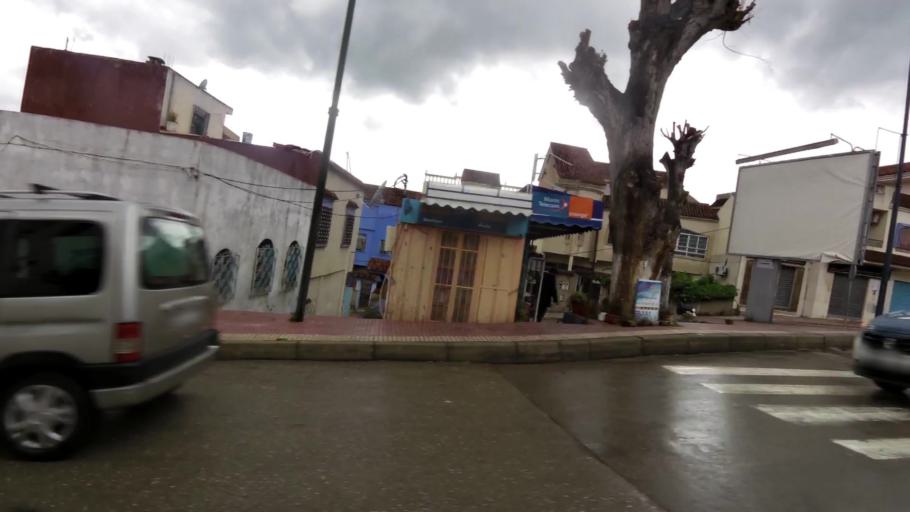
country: MA
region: Tanger-Tetouan
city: Chefchaouene
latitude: 35.1703
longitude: -5.2729
